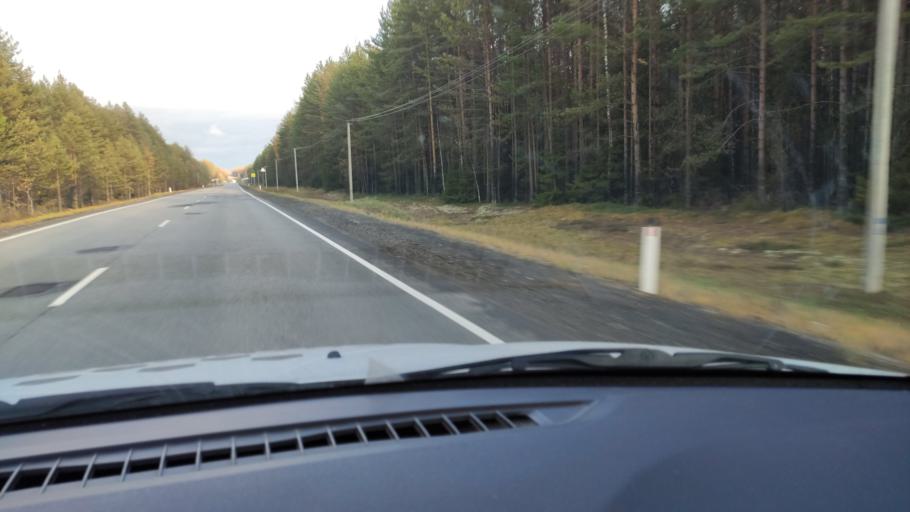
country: RU
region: Kirov
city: Belaya Kholunitsa
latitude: 58.9104
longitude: 51.0605
